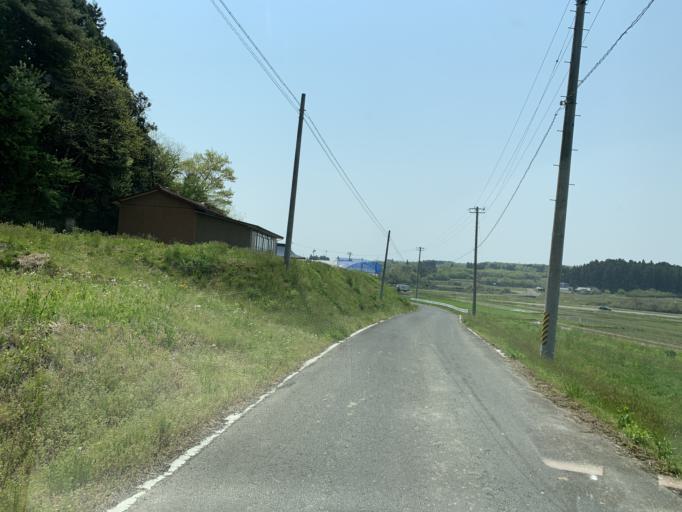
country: JP
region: Iwate
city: Ichinoseki
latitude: 38.8552
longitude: 141.0866
